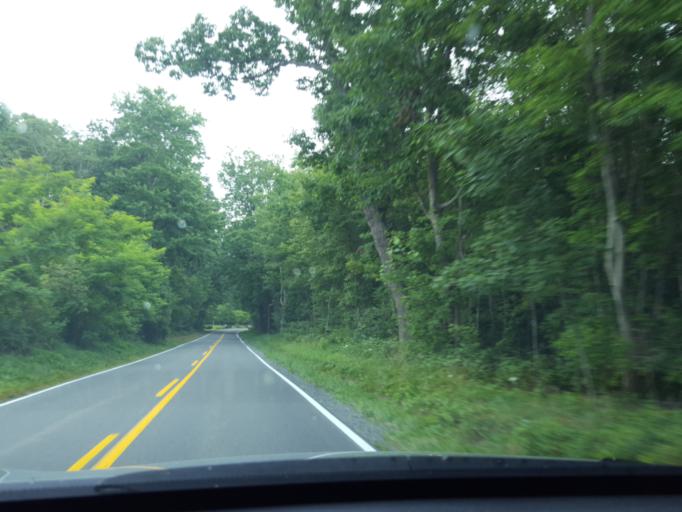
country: US
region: Virginia
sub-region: Spotsylvania County
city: Spotsylvania
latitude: 38.2697
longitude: -77.7994
